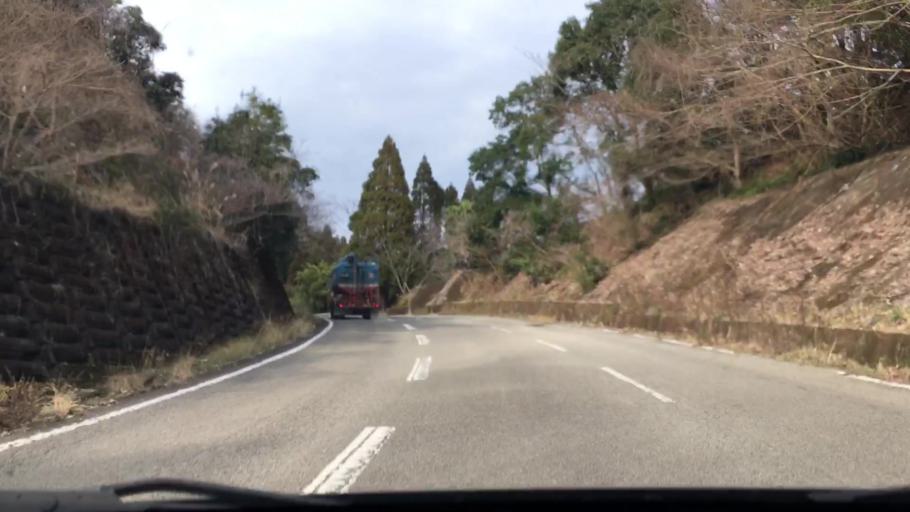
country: JP
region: Miyazaki
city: Nichinan
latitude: 31.6328
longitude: 131.3390
